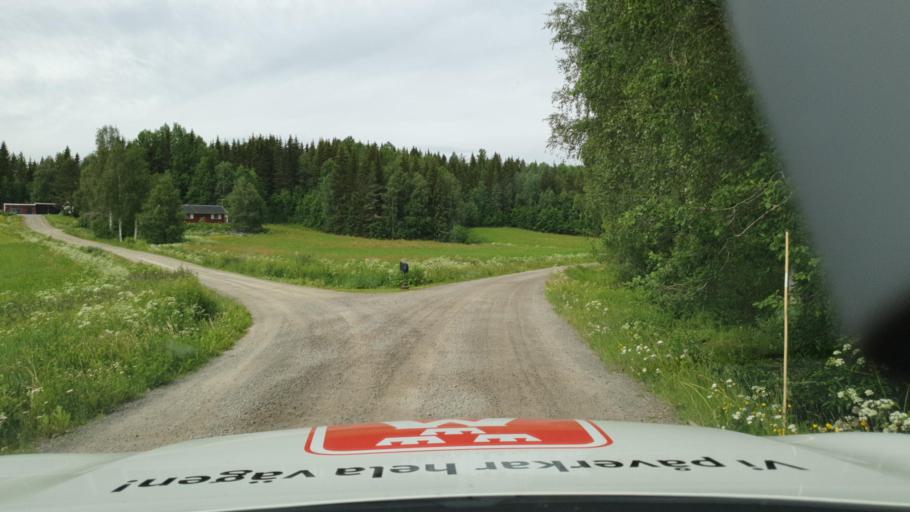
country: SE
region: Vaesterbotten
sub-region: Robertsfors Kommun
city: Robertsfors
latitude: 64.2631
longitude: 20.6284
